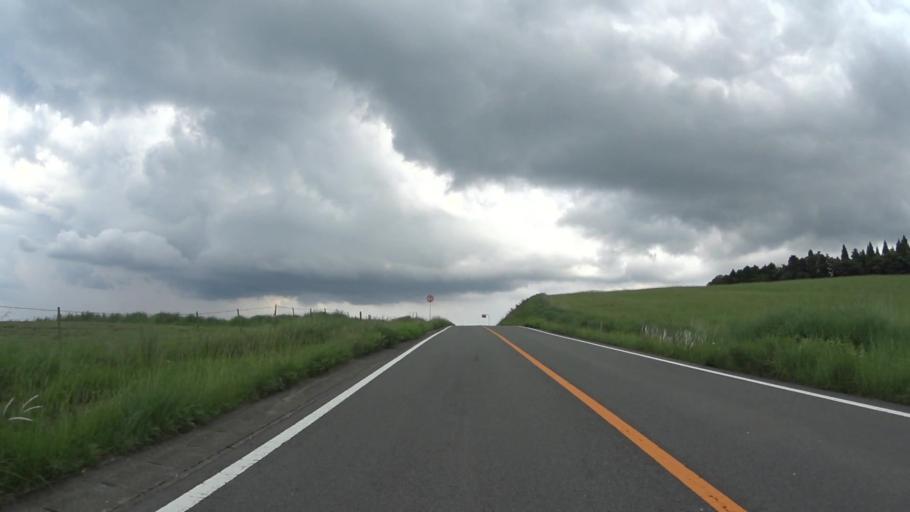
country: JP
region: Kumamoto
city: Aso
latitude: 32.9911
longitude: 131.1422
